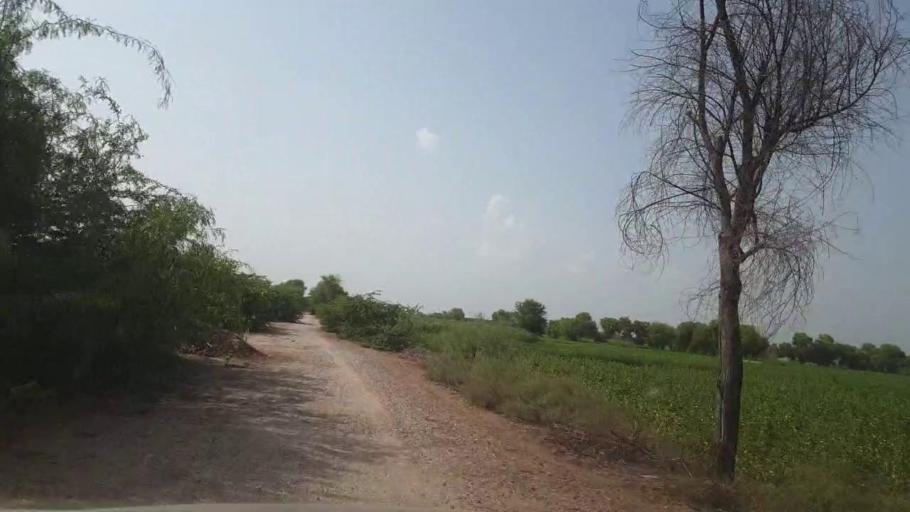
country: PK
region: Sindh
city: Pano Aqil
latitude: 27.7726
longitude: 69.1647
